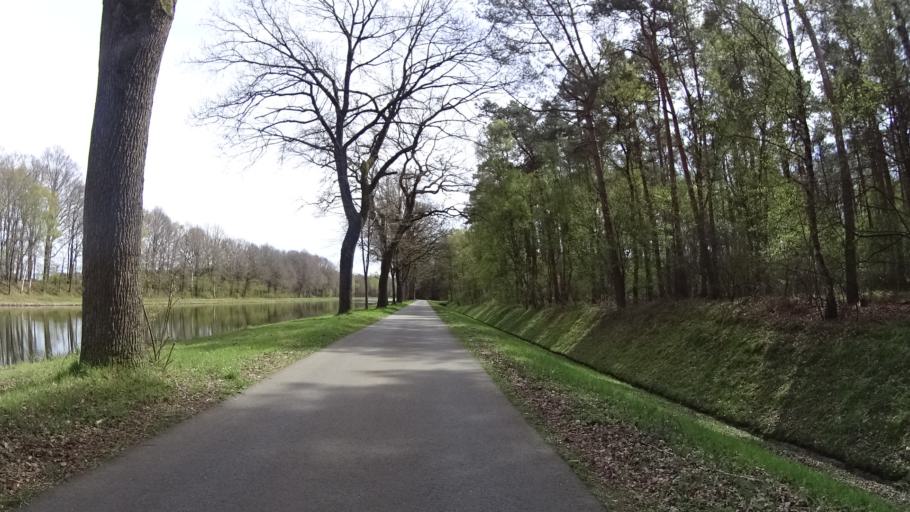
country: DE
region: Lower Saxony
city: Lunne
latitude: 52.4129
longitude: 7.3690
